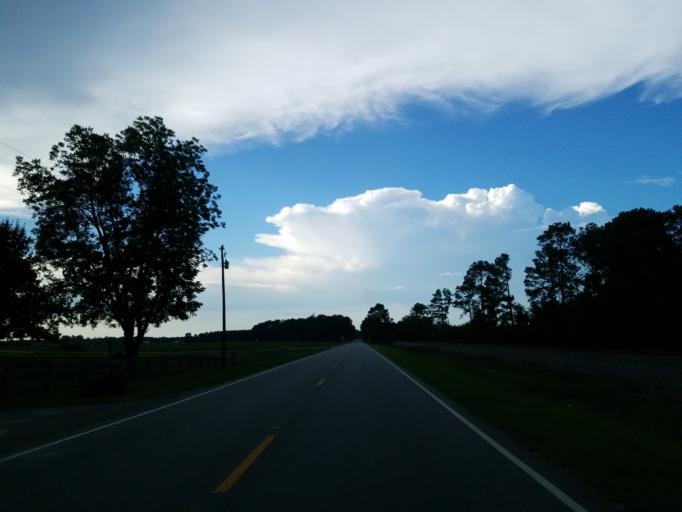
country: US
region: Georgia
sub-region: Tift County
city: Unionville
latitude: 31.3319
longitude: -83.4797
